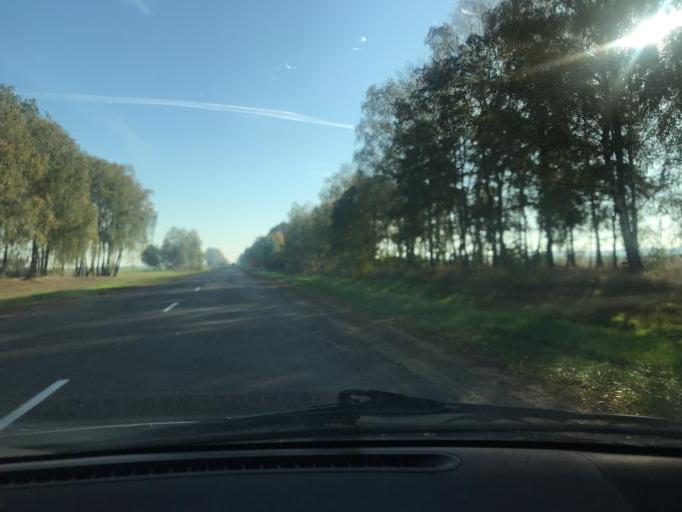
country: BY
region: Brest
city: Ivanava
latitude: 52.1457
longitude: 25.4705
